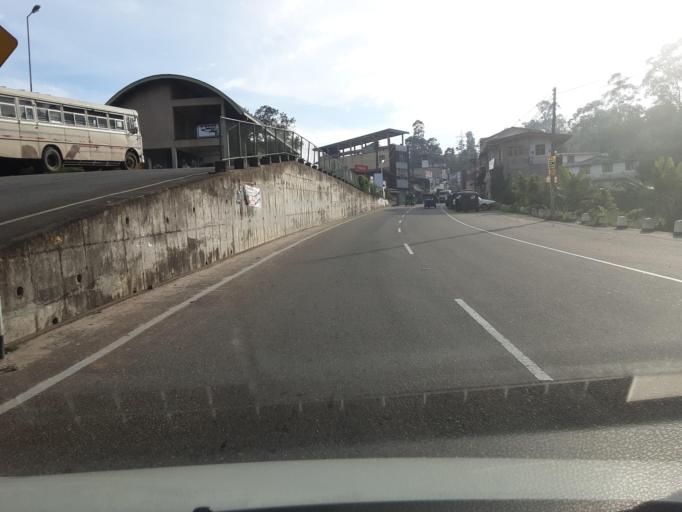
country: LK
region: Uva
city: Badulla
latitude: 6.9359
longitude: 80.9879
